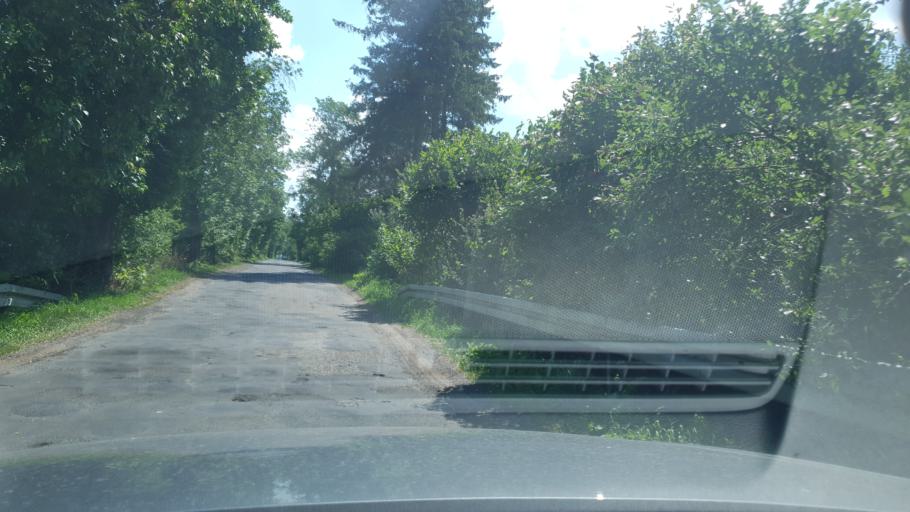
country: PL
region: Kujawsko-Pomorskie
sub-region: Powiat wabrzeski
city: Pluznica
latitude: 53.3574
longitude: 18.8177
